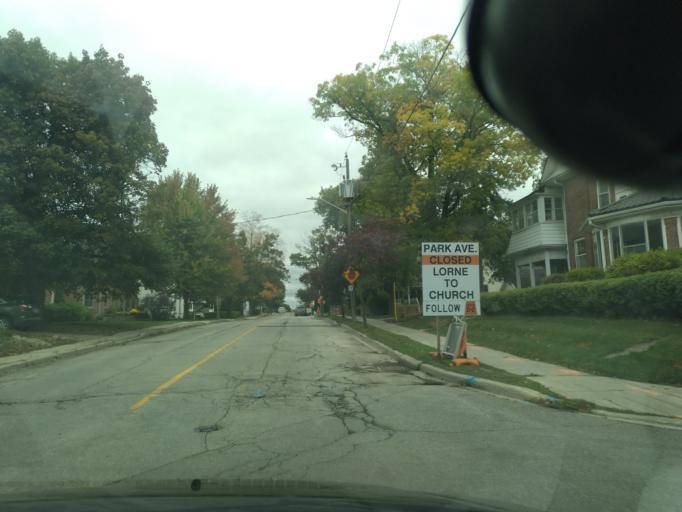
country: CA
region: Ontario
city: Newmarket
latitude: 44.0516
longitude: -79.4638
